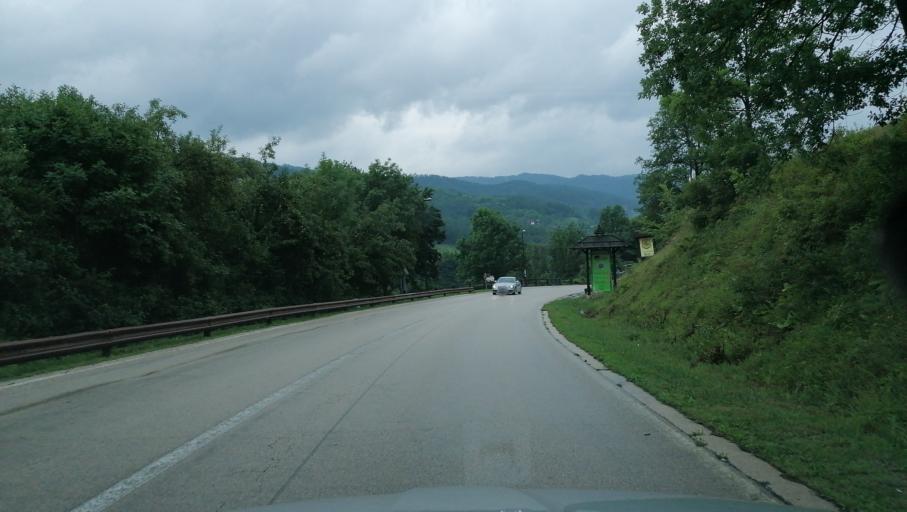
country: RS
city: Durici
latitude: 43.7947
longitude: 19.5123
